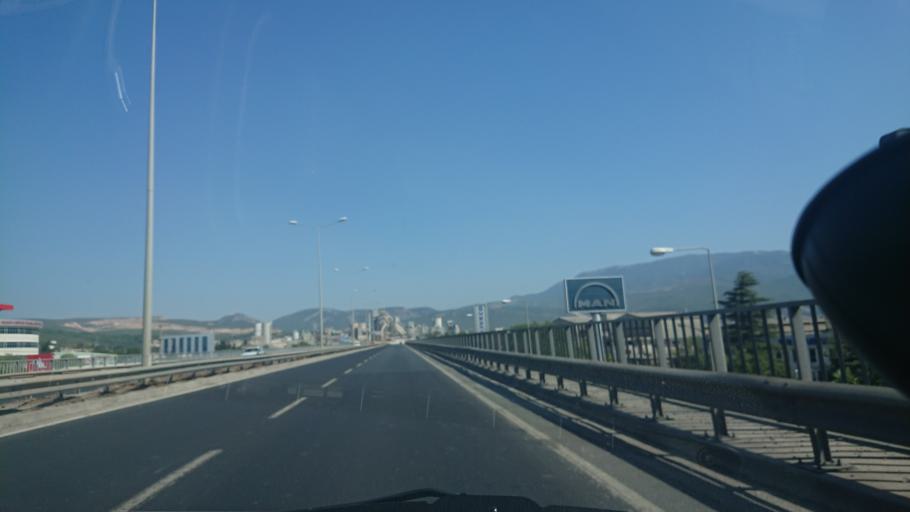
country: TR
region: Izmir
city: Bornova
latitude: 38.4582
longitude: 27.2475
